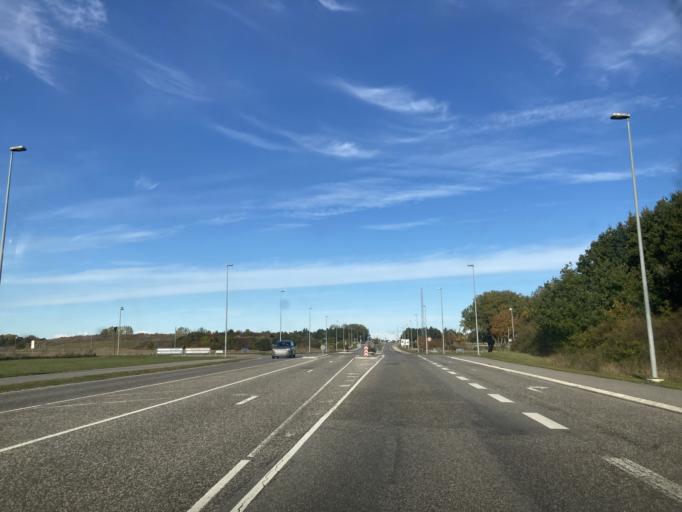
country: DK
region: Capital Region
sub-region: Vallensbaek Kommune
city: Vallensbaek
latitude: 55.6383
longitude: 12.3736
